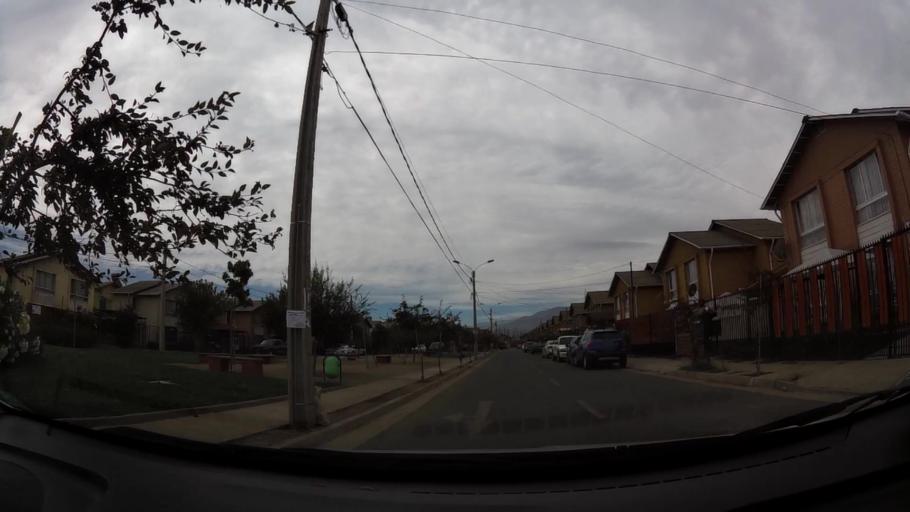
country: CL
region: O'Higgins
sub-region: Provincia de Cachapoal
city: Rancagua
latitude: -34.1306
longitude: -70.7322
